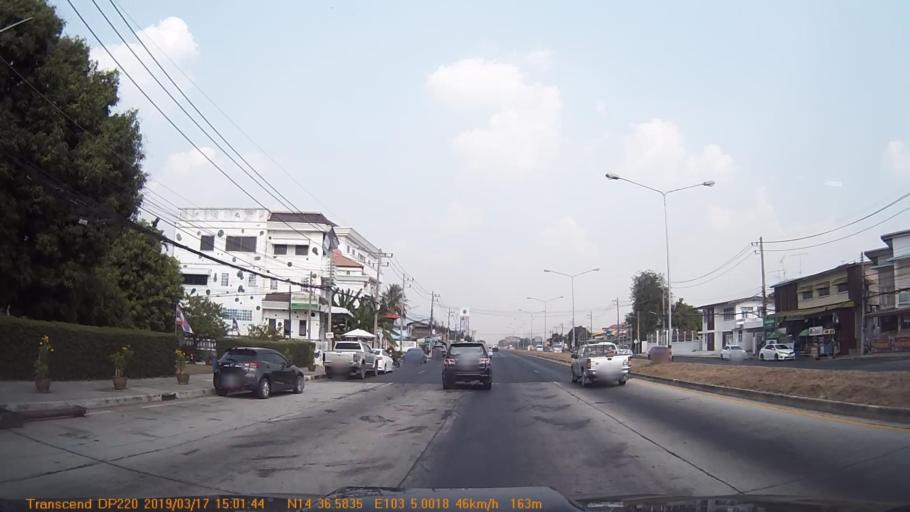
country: TH
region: Buriram
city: Prakhon Chai
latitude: 14.6097
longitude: 103.0835
